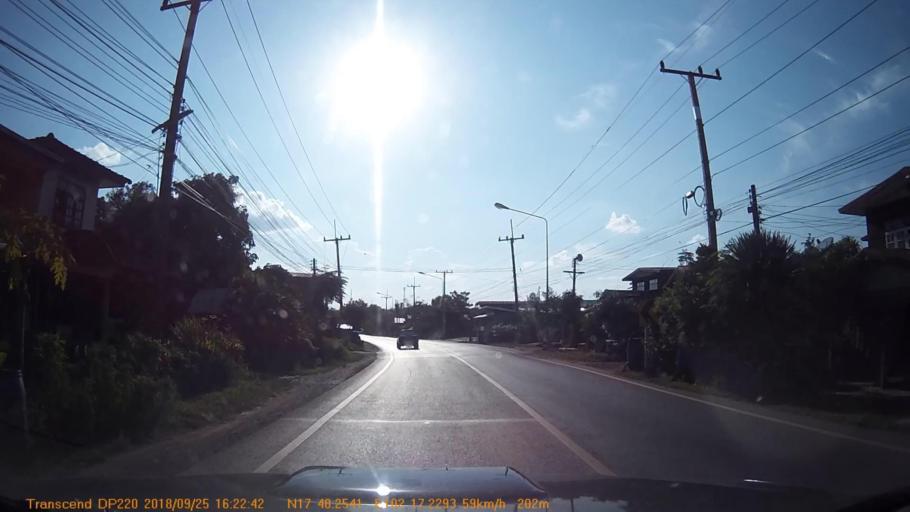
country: TH
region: Changwat Udon Thani
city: Nam Som
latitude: 17.8042
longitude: 102.2872
